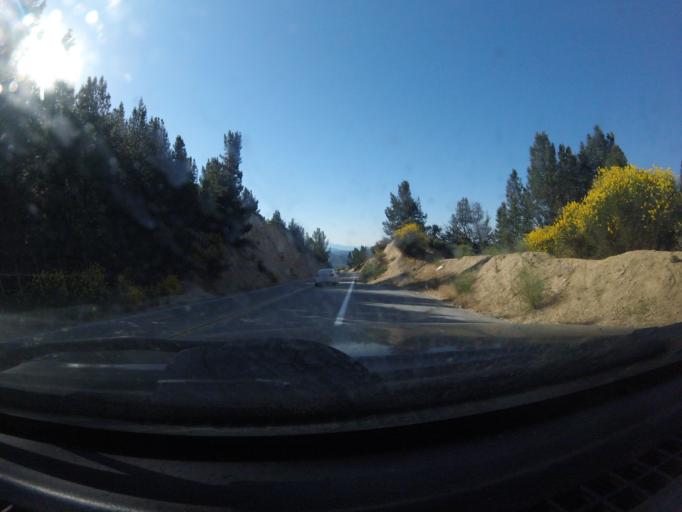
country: US
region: California
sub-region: San Bernardino County
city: Running Springs
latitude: 34.1905
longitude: -117.1568
